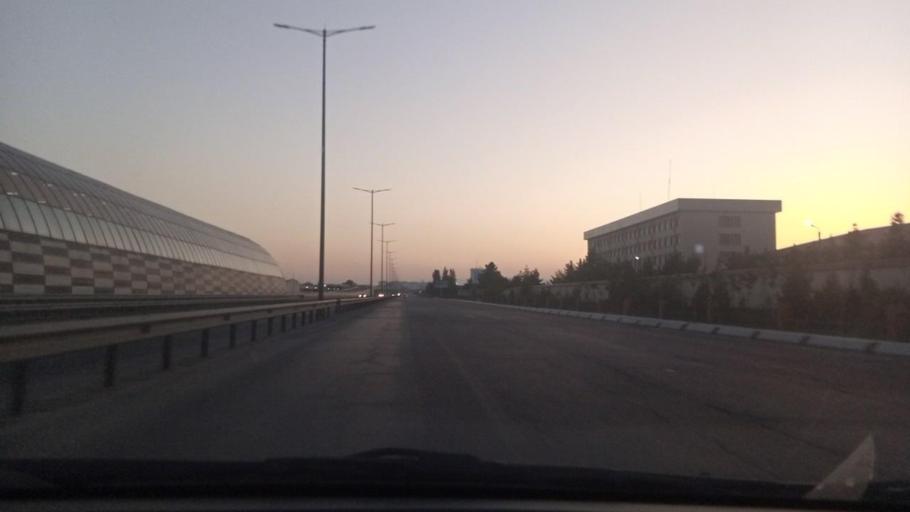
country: UZ
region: Toshkent Shahri
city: Bektemir
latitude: 41.2559
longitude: 69.3588
